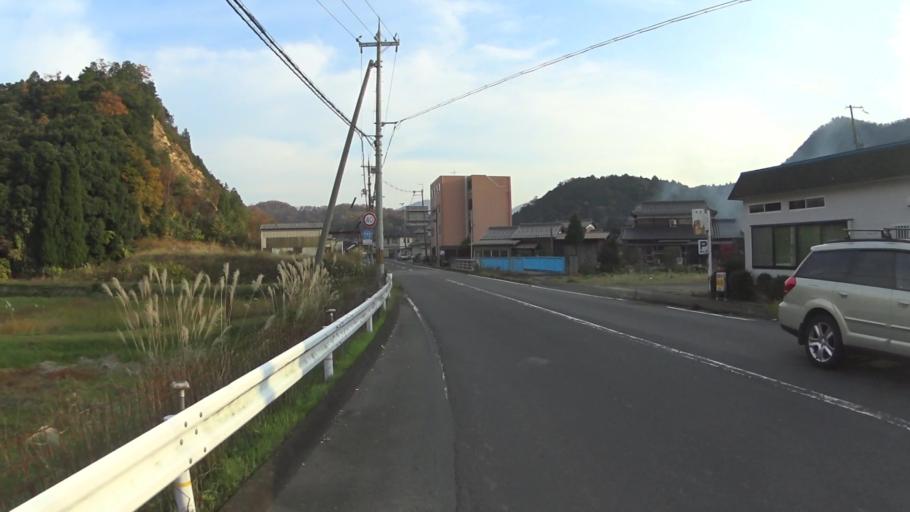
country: JP
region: Kyoto
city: Maizuru
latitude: 35.5001
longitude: 135.4323
